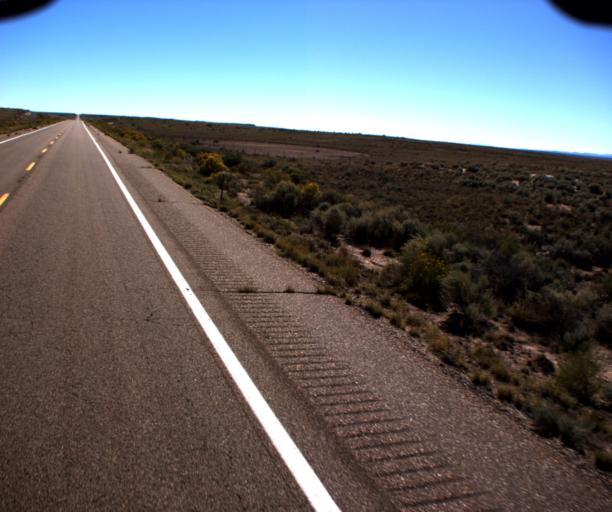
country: US
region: Arizona
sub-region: Navajo County
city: Holbrook
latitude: 34.7883
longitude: -109.8806
